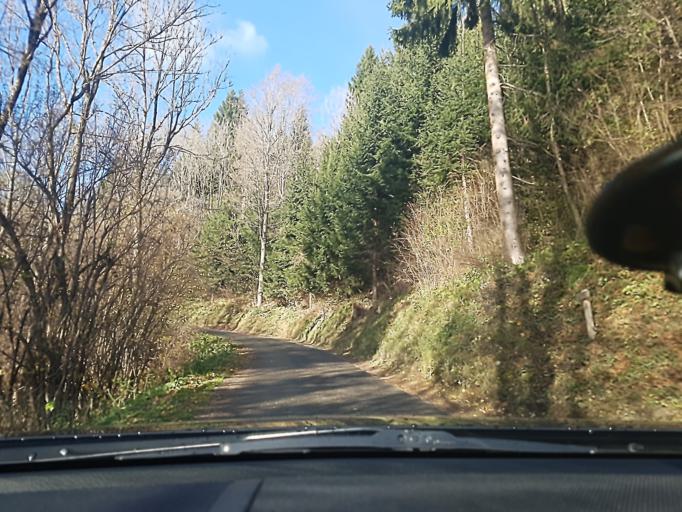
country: AT
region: Styria
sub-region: Politischer Bezirk Murtal
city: Oberzeiring
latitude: 47.2533
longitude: 14.4565
